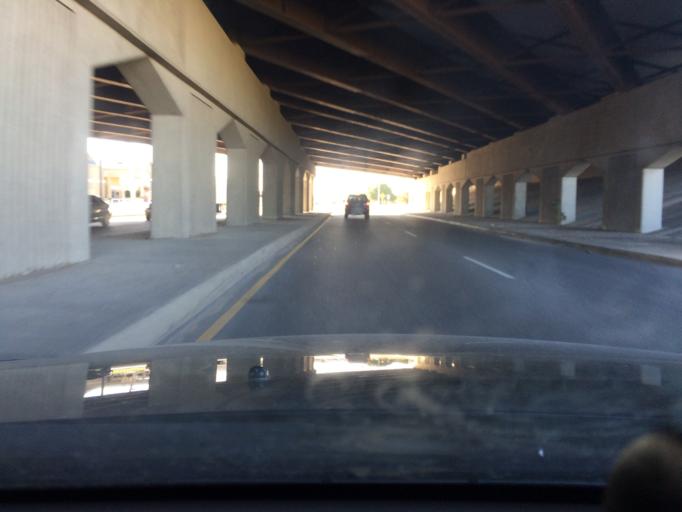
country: US
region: Oklahoma
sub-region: Tulsa County
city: Broken Arrow
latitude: 36.0900
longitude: -95.8368
